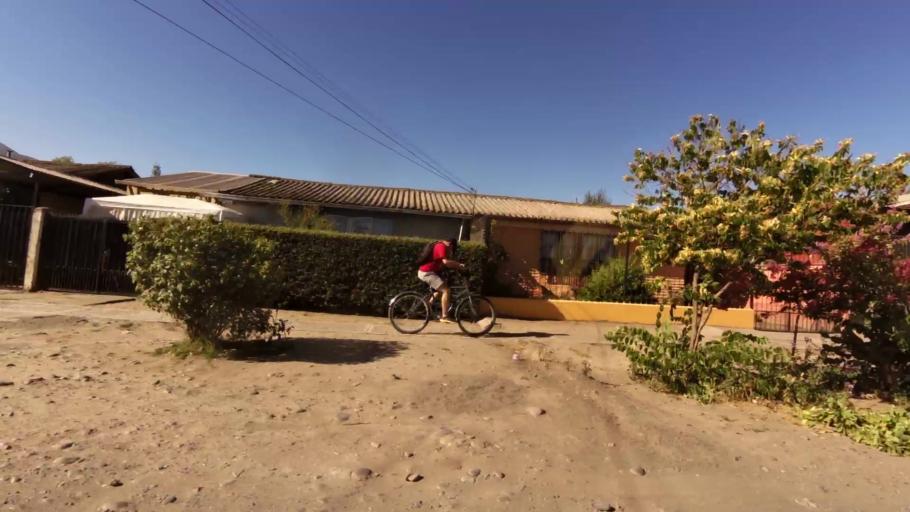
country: CL
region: O'Higgins
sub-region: Provincia de Colchagua
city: Chimbarongo
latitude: -34.5745
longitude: -70.9954
